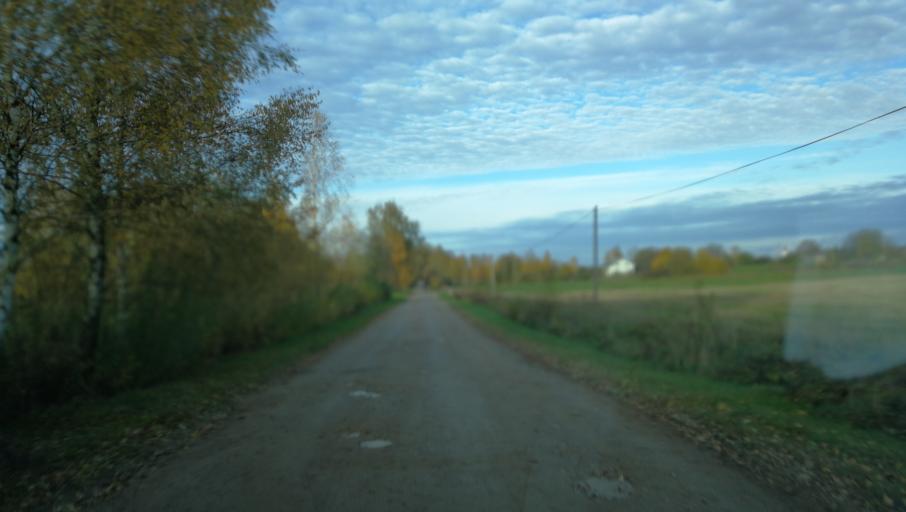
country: LV
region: Cesu Rajons
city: Cesis
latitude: 57.2974
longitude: 25.2491
